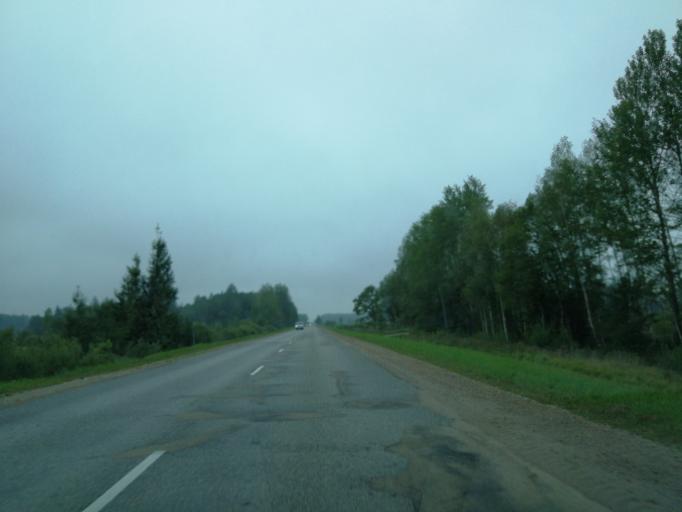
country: LV
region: Varkava
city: Vecvarkava
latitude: 56.3176
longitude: 26.4680
